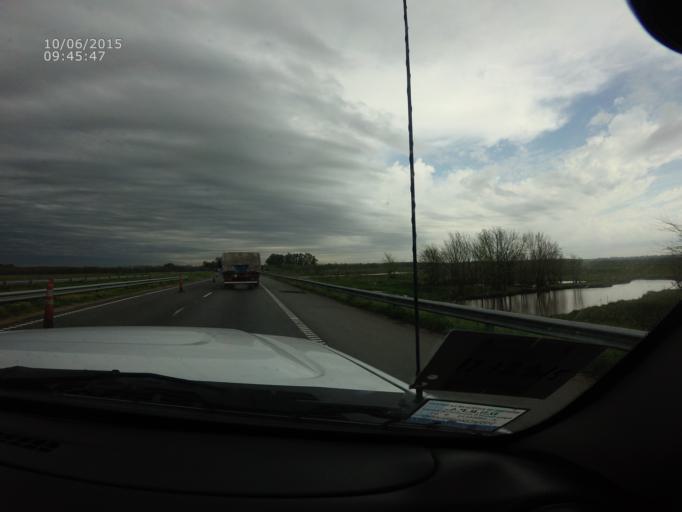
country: AR
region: Buenos Aires
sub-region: San Antonio de Areco
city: San Antonio de Areco
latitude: -34.0575
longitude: -59.2961
